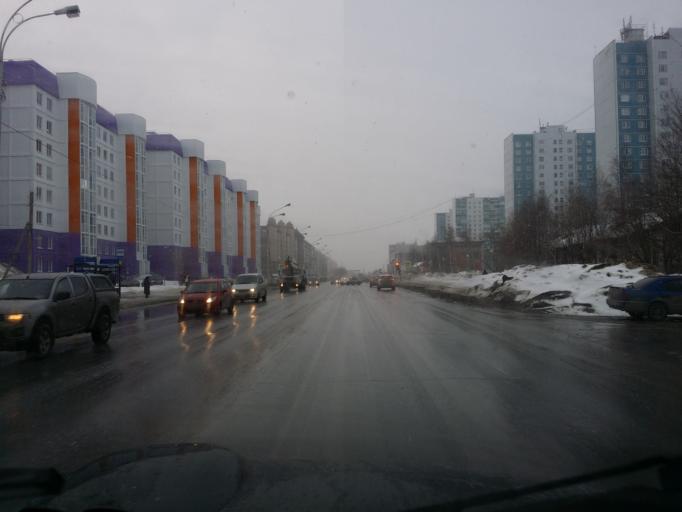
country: RU
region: Khanty-Mansiyskiy Avtonomnyy Okrug
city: Nizhnevartovsk
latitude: 60.9292
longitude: 76.5773
